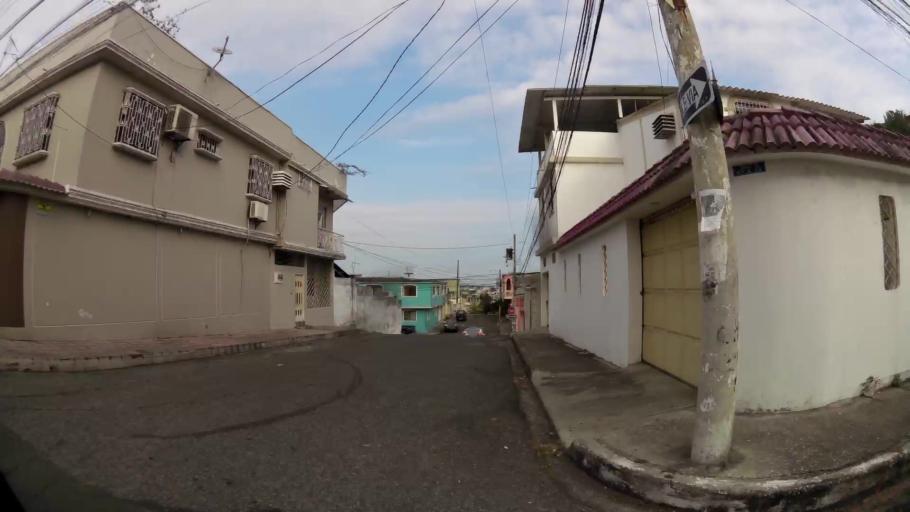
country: EC
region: Guayas
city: Eloy Alfaro
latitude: -2.1336
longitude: -79.8923
